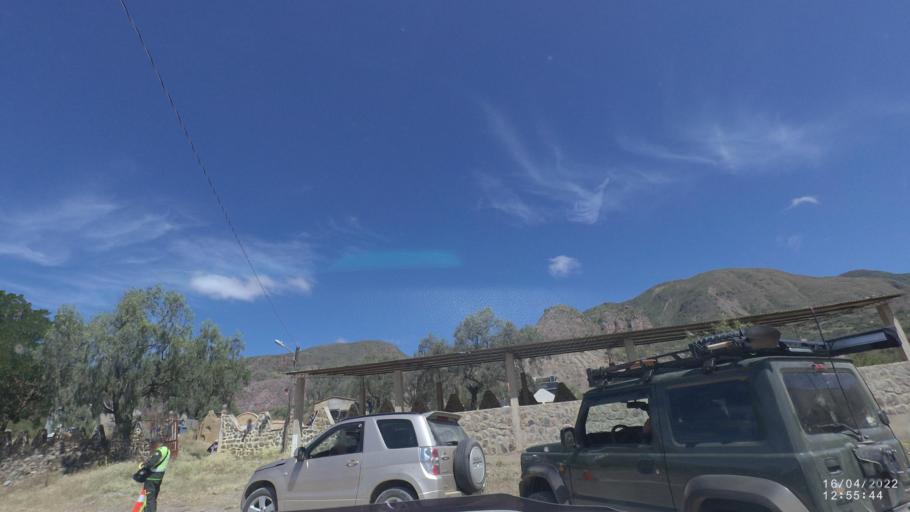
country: BO
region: Cochabamba
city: Mizque
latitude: -17.9880
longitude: -65.6288
